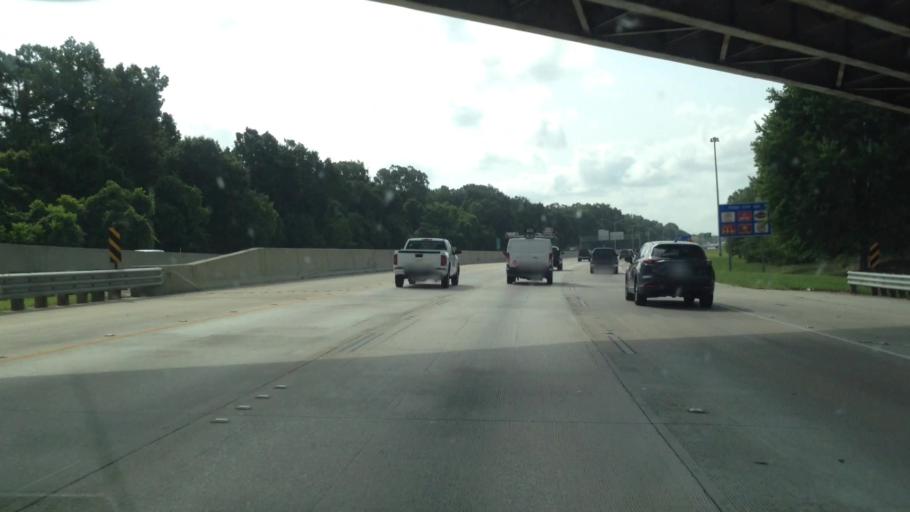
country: US
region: Louisiana
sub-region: East Baton Rouge Parish
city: Westminster
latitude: 30.4168
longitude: -91.1139
